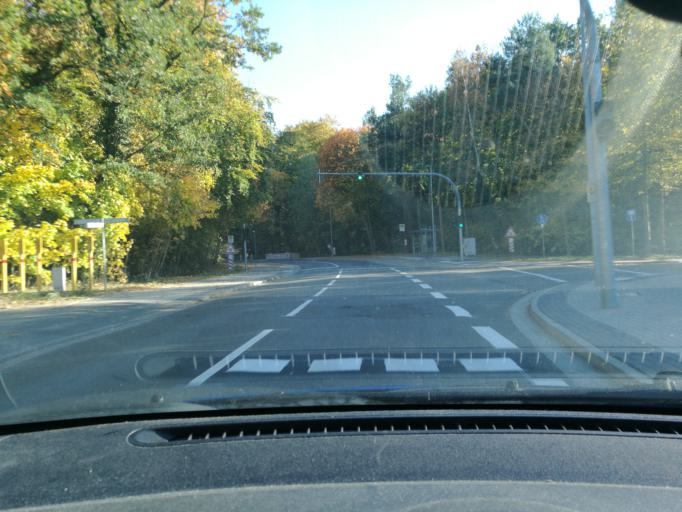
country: DE
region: Lower Saxony
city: Lueneburg
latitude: 53.2621
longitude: 10.4259
